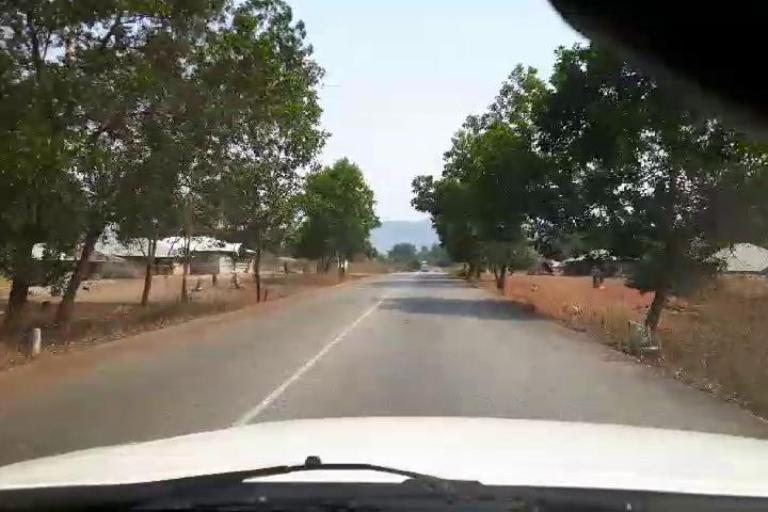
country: SL
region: Northern Province
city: Yonibana
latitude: 8.4016
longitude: -12.1956
